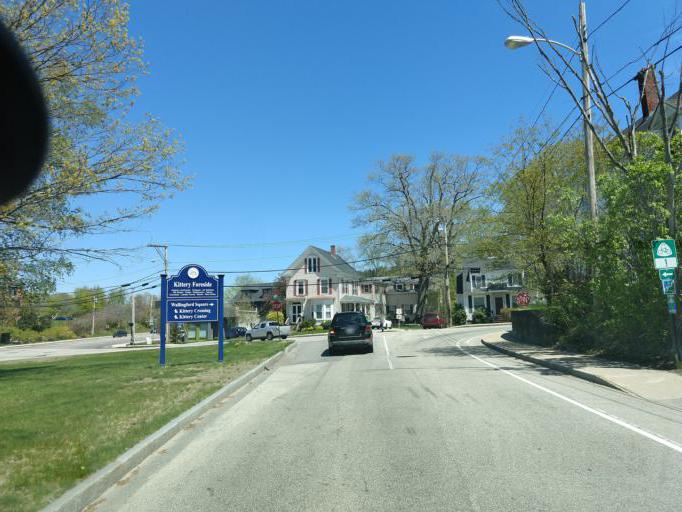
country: US
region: Maine
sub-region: York County
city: Kittery
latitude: 43.0855
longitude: -70.7499
